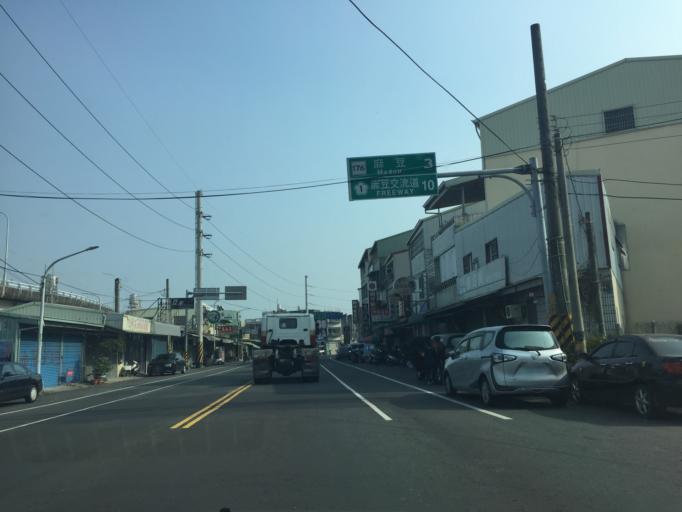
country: TW
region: Taiwan
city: Xinying
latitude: 23.1976
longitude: 120.3175
